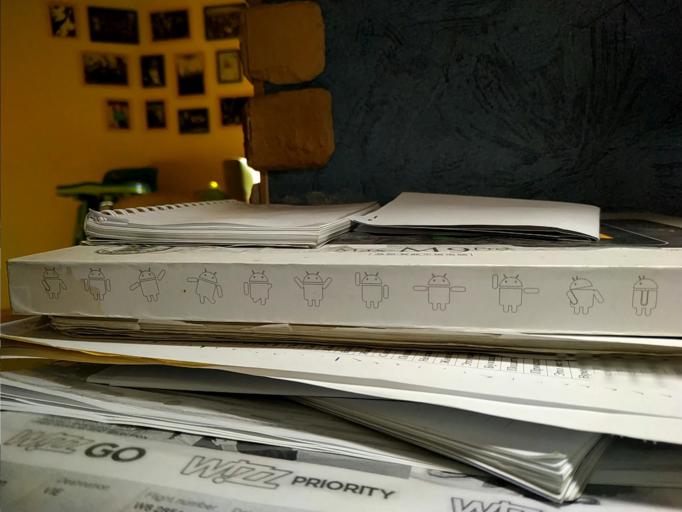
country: RU
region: Novgorod
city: Poddor'ye
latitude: 57.3237
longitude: 31.1914
